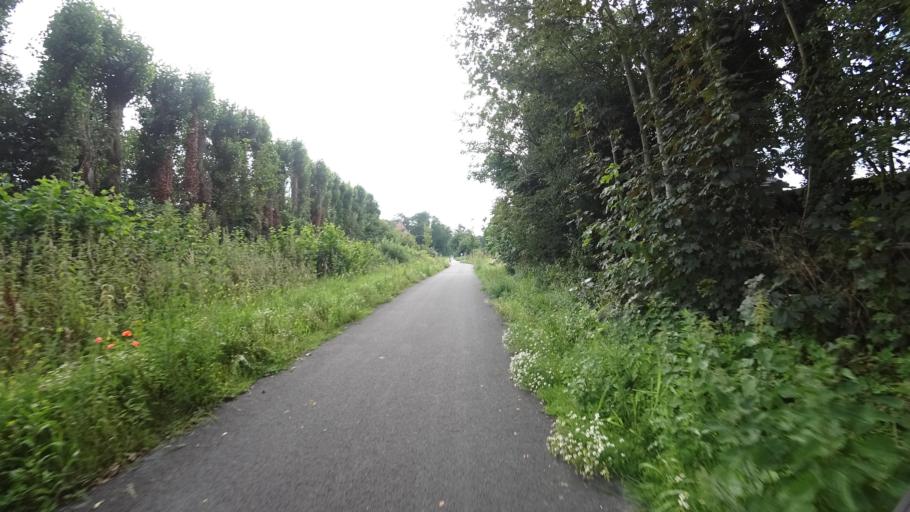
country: BE
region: Flanders
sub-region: Provincie West-Vlaanderen
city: Damme
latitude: 51.2048
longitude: 3.3135
